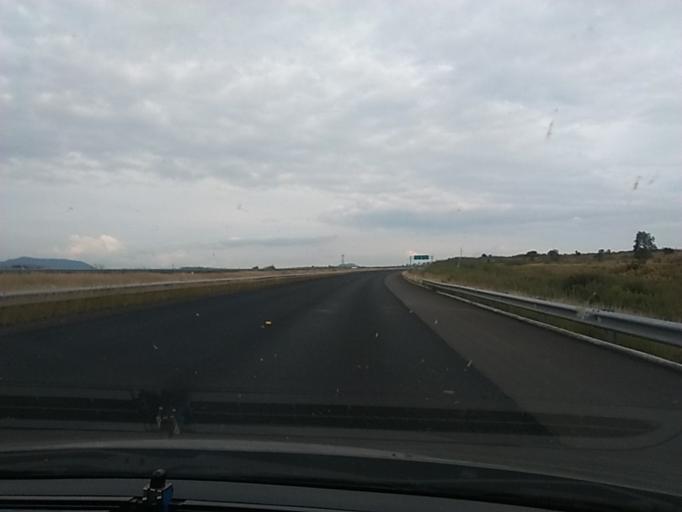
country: MX
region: Mexico
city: Huaniqueo de Morales
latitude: 19.8884
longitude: -101.5203
